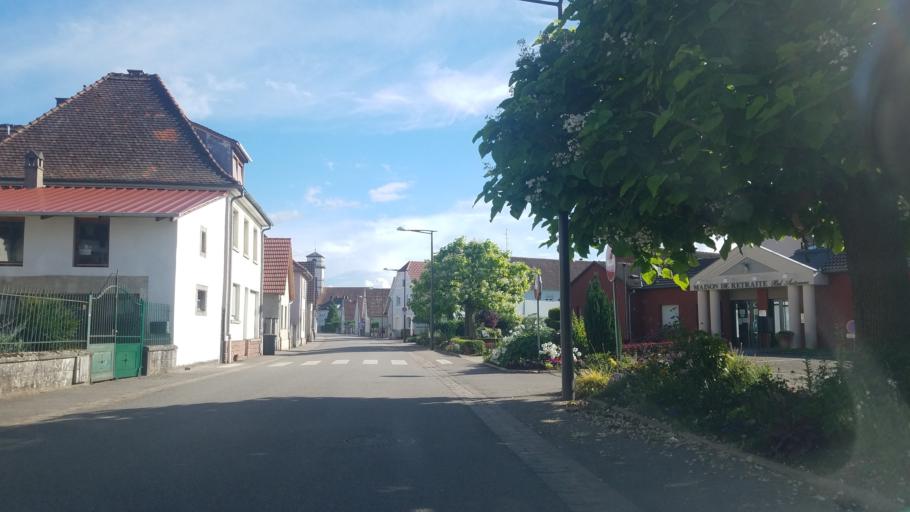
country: FR
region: Alsace
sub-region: Departement du Bas-Rhin
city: Drusenheim
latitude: 48.7676
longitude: 7.9517
